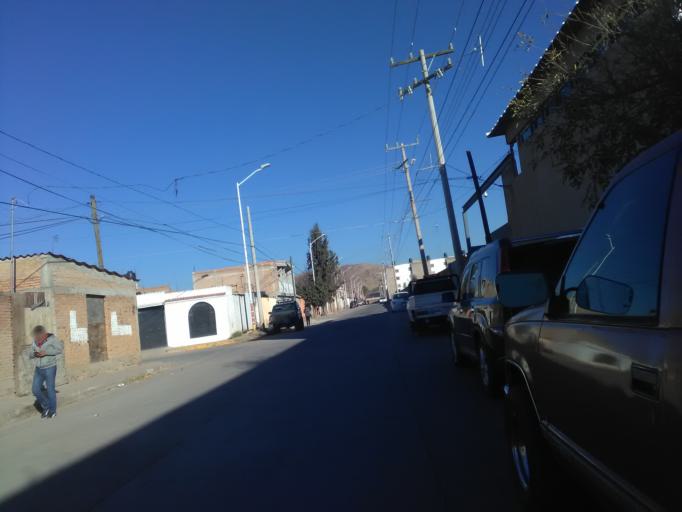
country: MX
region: Durango
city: Victoria de Durango
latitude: 24.0533
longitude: -104.6526
